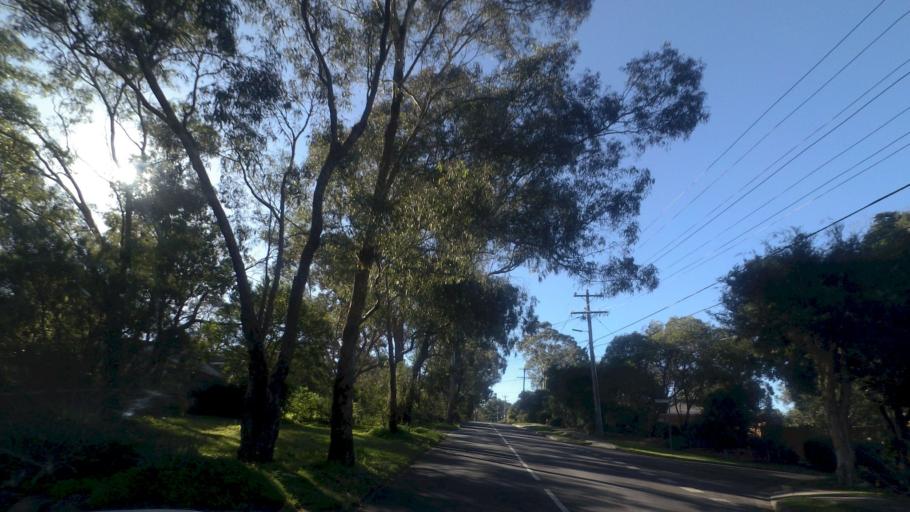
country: AU
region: Victoria
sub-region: Nillumbik
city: Eltham North
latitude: -37.7098
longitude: 145.1603
